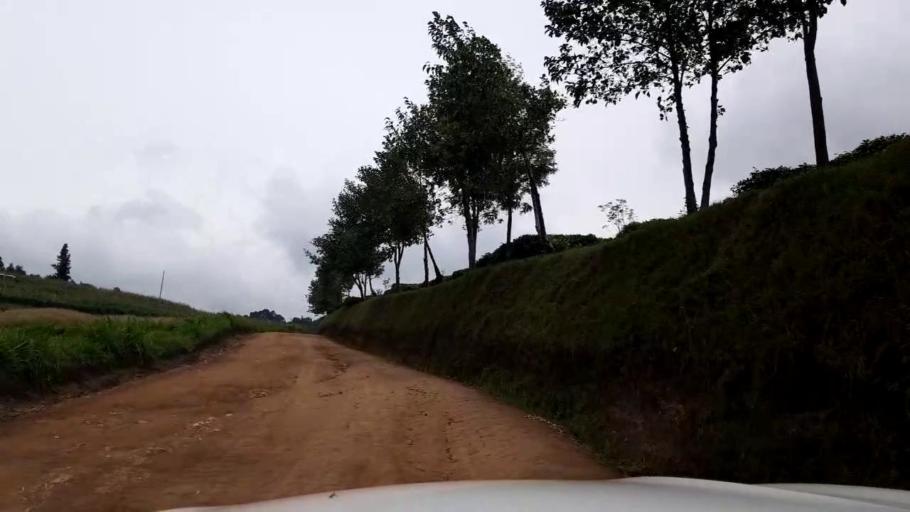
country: RW
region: Western Province
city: Kibuye
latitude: -1.9548
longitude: 29.4045
